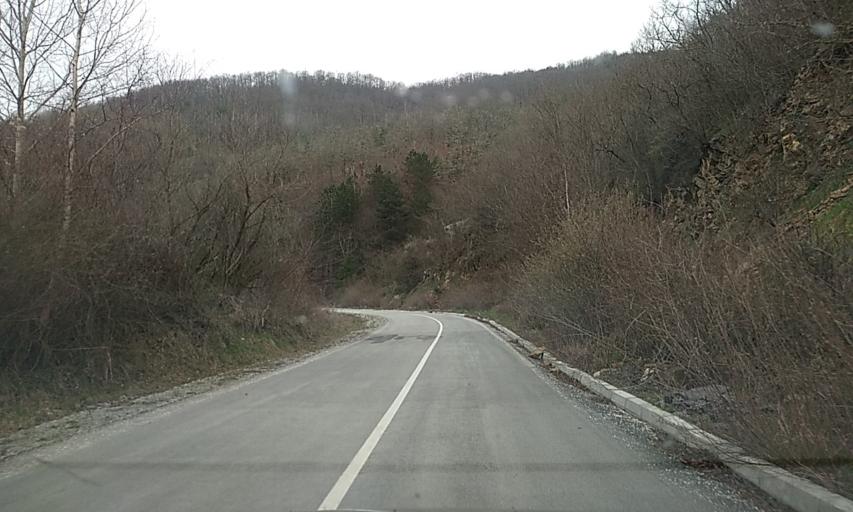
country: RS
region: Central Serbia
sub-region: Pcinjski Okrug
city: Bosilegrad
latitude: 42.3918
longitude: 22.4523
